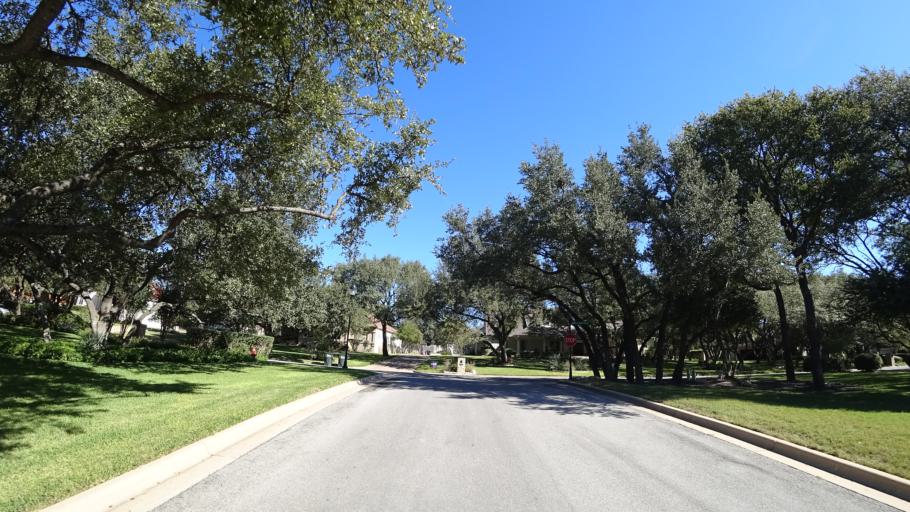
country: US
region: Texas
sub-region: Travis County
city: West Lake Hills
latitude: 30.3318
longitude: -97.7868
